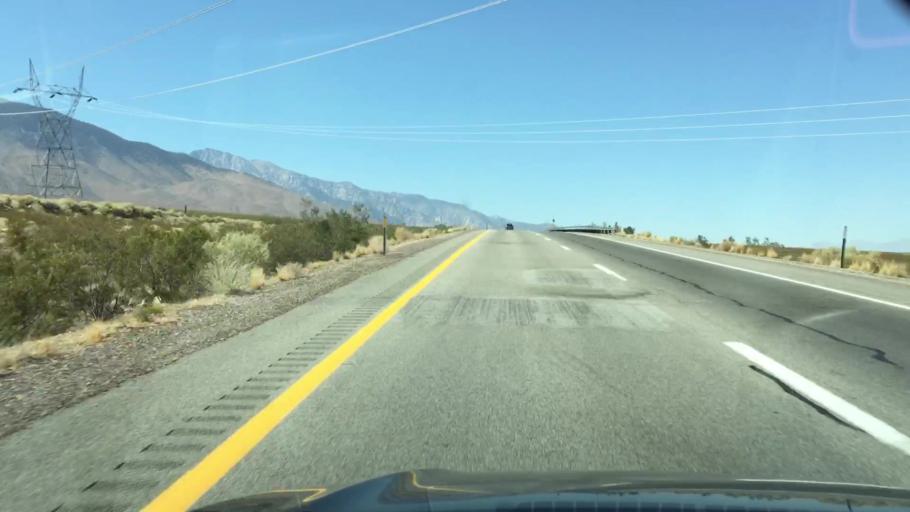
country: US
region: California
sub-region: Kern County
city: Inyokern
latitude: 36.1074
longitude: -117.9690
